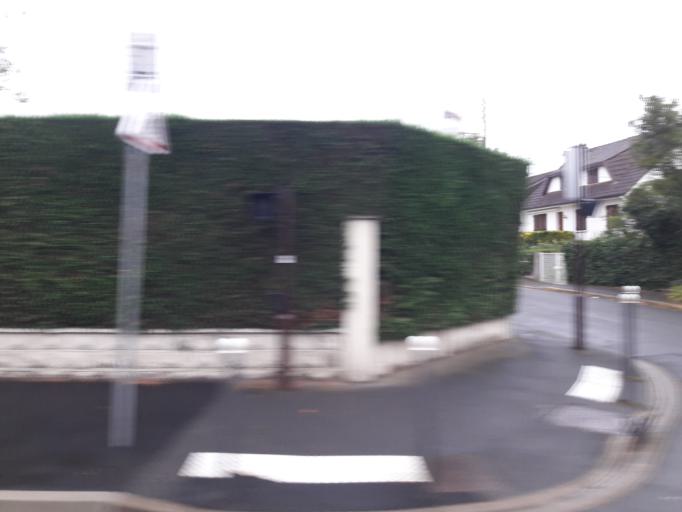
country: FR
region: Ile-de-France
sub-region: Departement de l'Essonne
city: Epinay-sur-Orge
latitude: 48.6784
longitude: 2.3182
